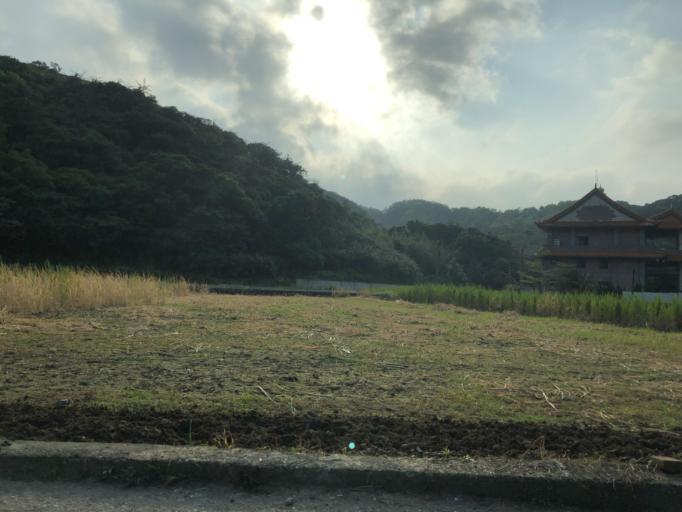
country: TW
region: Taiwan
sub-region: Keelung
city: Keelung
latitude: 25.2049
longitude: 121.6482
